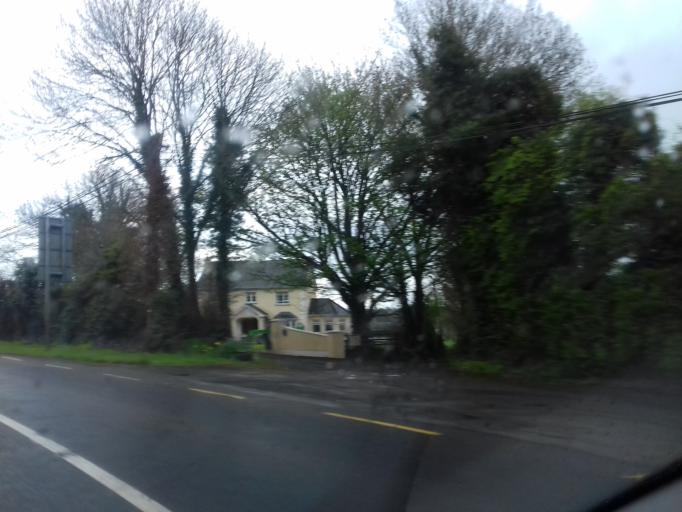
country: IE
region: Ulster
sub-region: An Cabhan
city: Ballyconnell
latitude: 54.1190
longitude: -7.6706
